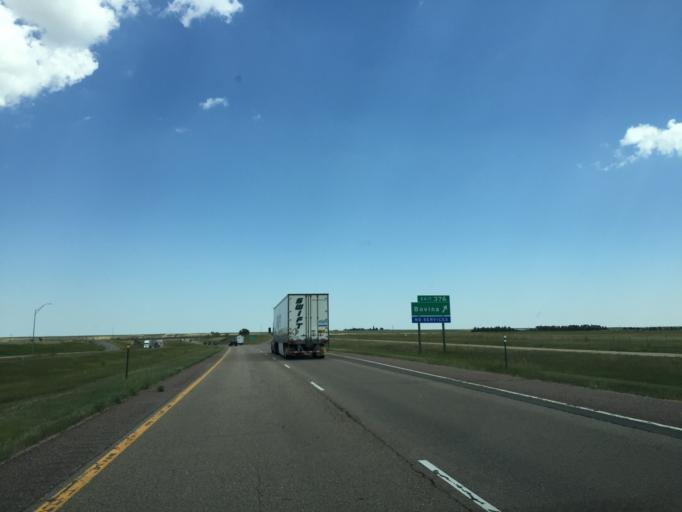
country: US
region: Colorado
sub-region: Lincoln County
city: Hugo
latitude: 39.2787
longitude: -103.4044
